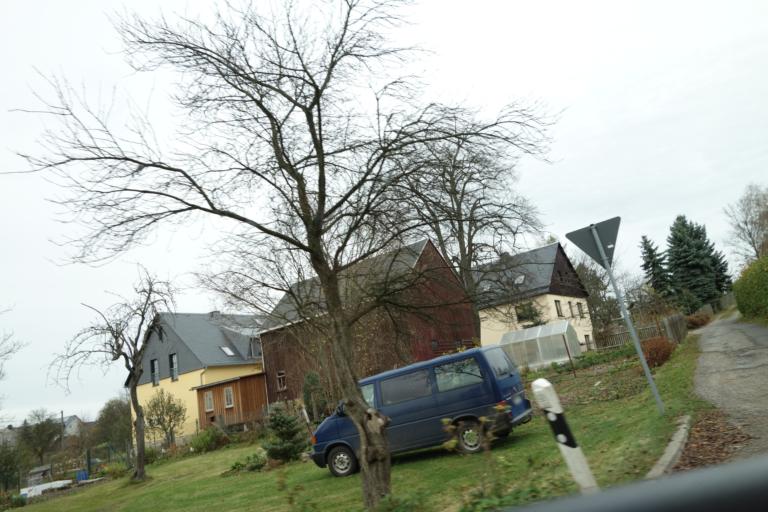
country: DE
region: Saxony
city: Leubsdorf
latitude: 50.7985
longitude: 13.1811
